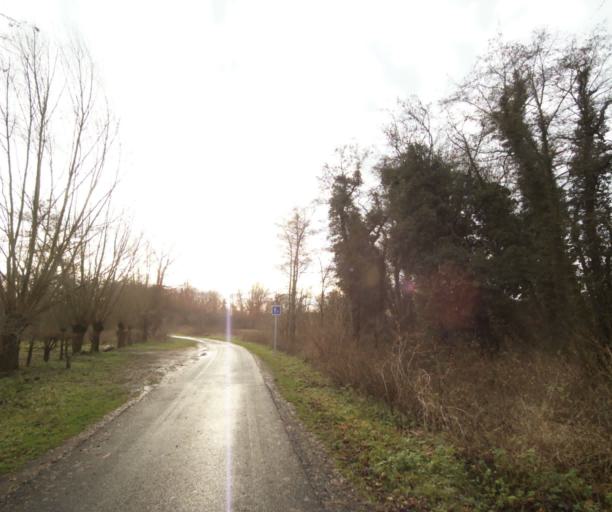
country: FR
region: Nord-Pas-de-Calais
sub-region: Departement du Nord
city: Hergnies
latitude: 50.4666
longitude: 3.5309
